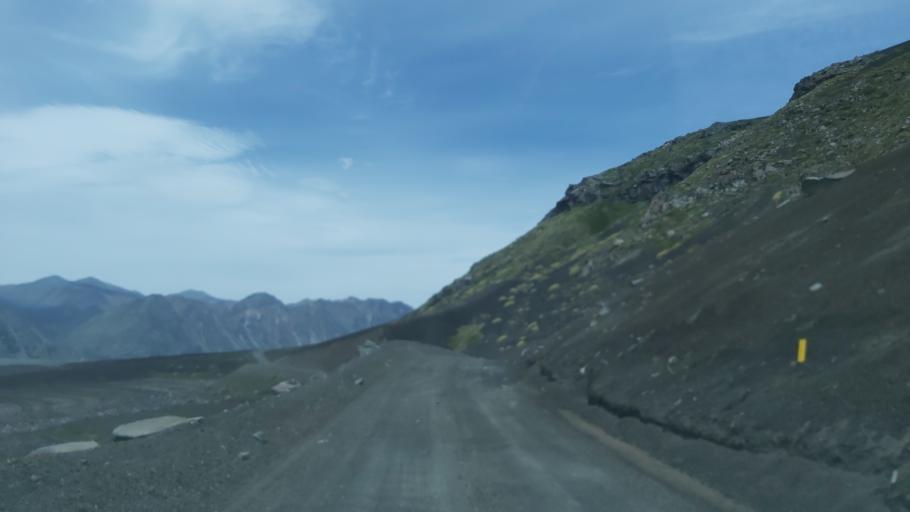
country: AR
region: Neuquen
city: Andacollo
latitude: -37.4080
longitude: -71.2976
